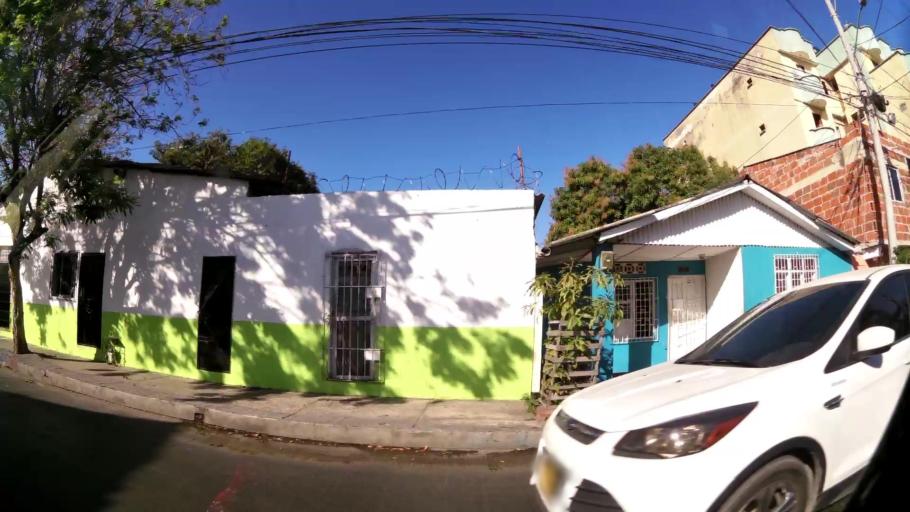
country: CO
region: Atlantico
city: Barranquilla
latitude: 10.9683
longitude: -74.7868
